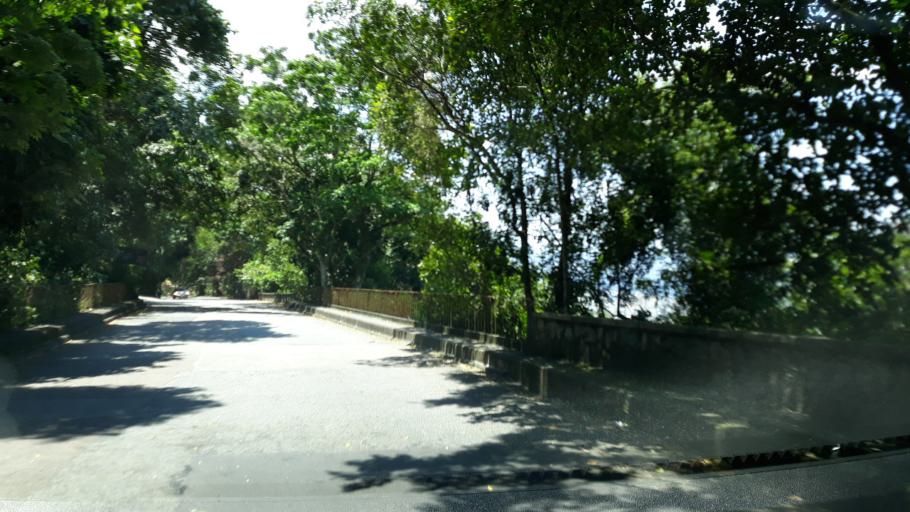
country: BR
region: Rio de Janeiro
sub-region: Rio De Janeiro
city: Rio de Janeiro
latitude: -22.9459
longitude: -43.2054
